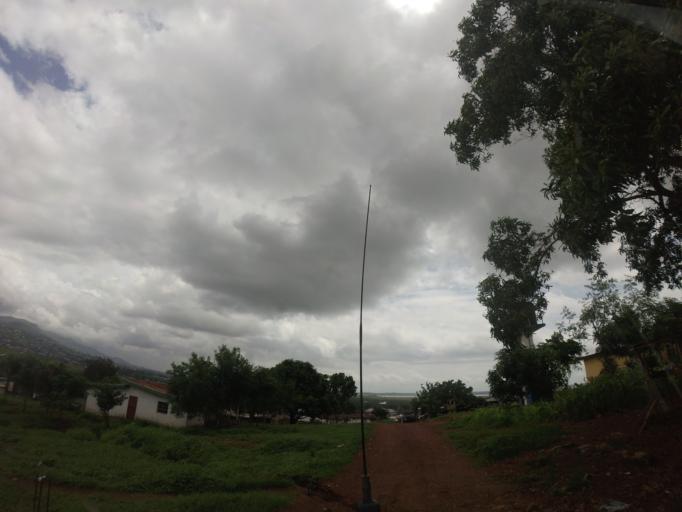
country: SL
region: Western Area
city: Hastings
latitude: 8.3870
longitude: -13.1244
